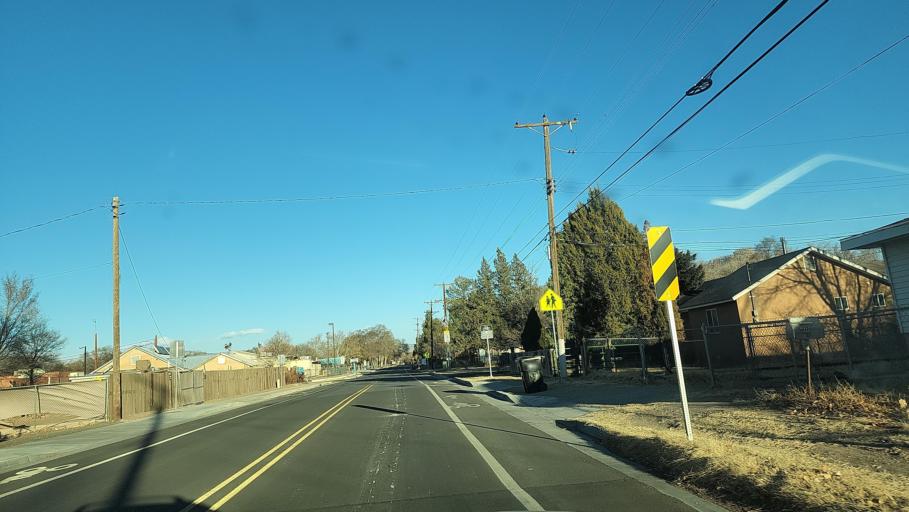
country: US
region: New Mexico
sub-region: Bernalillo County
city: South Valley
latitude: 35.0306
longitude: -106.6952
